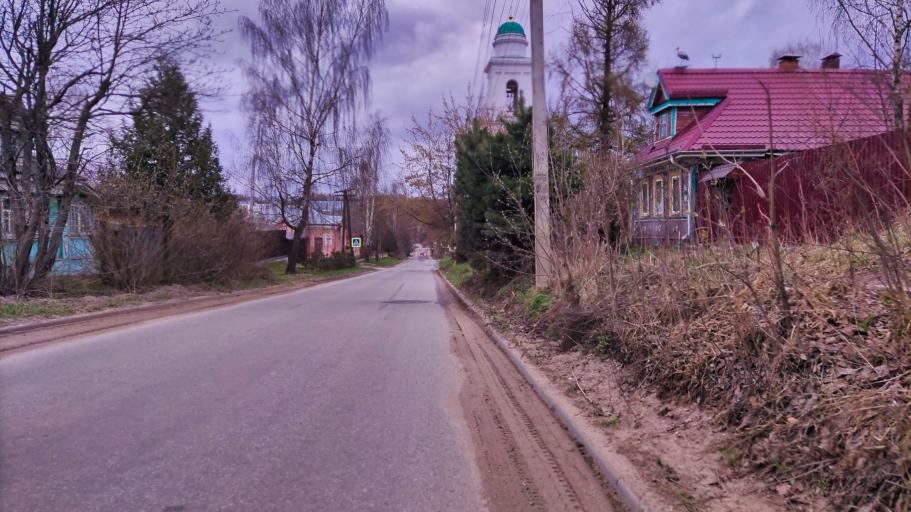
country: RU
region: Tverskaya
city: Rzhev
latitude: 56.2541
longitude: 34.3357
